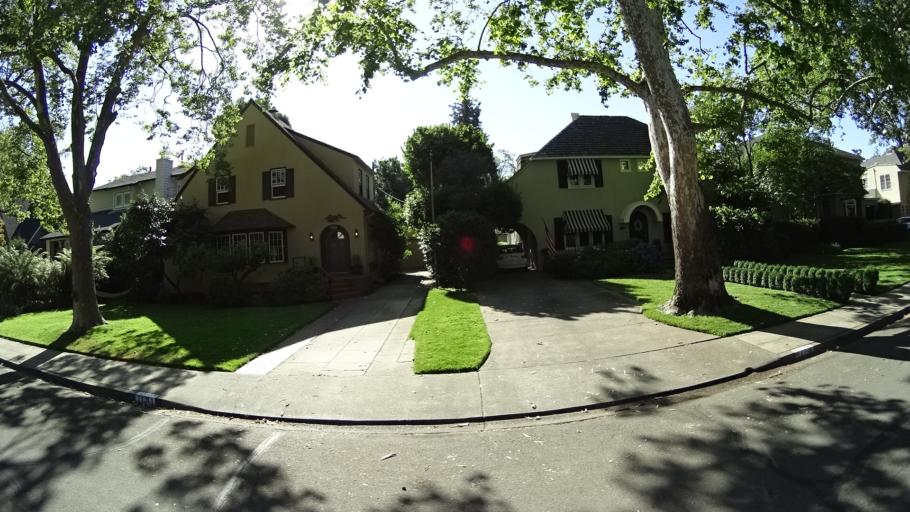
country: US
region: California
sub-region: Sacramento County
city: Sacramento
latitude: 38.5679
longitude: -121.4522
